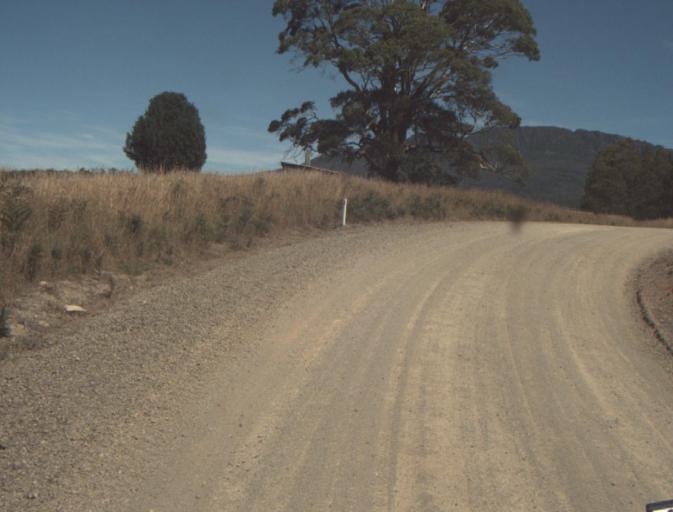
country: AU
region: Tasmania
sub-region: Dorset
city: Scottsdale
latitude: -41.3271
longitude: 147.4443
